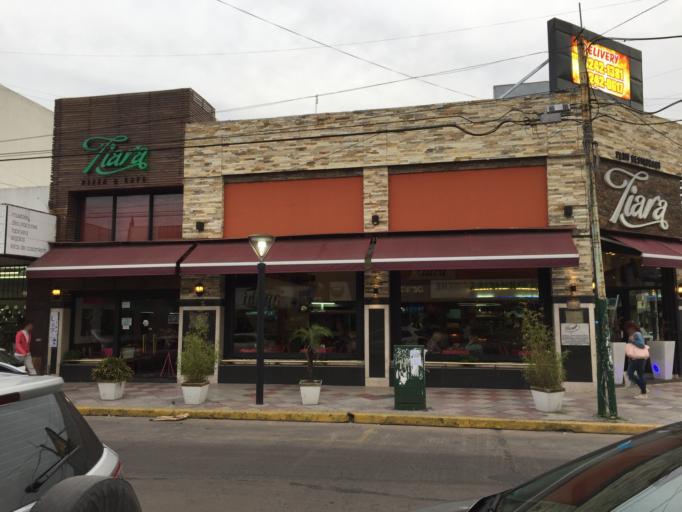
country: AR
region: Buenos Aires
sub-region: Partido de Lomas de Zamora
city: Lomas de Zamora
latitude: -34.7433
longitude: -58.3931
